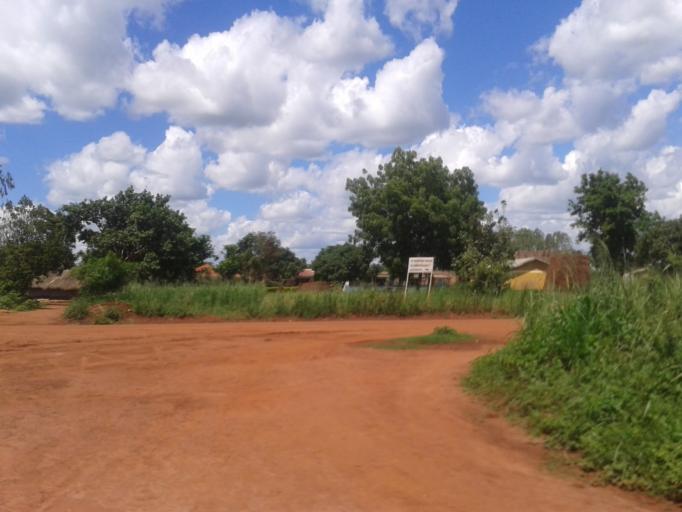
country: UG
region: Northern Region
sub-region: Gulu District
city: Gulu
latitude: 2.7600
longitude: 32.3231
